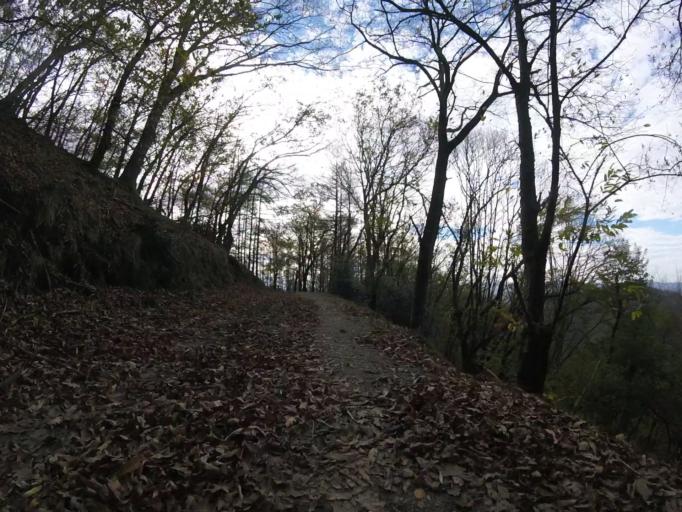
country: ES
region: Navarre
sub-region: Provincia de Navarra
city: Arano
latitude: 43.2411
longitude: -1.8482
